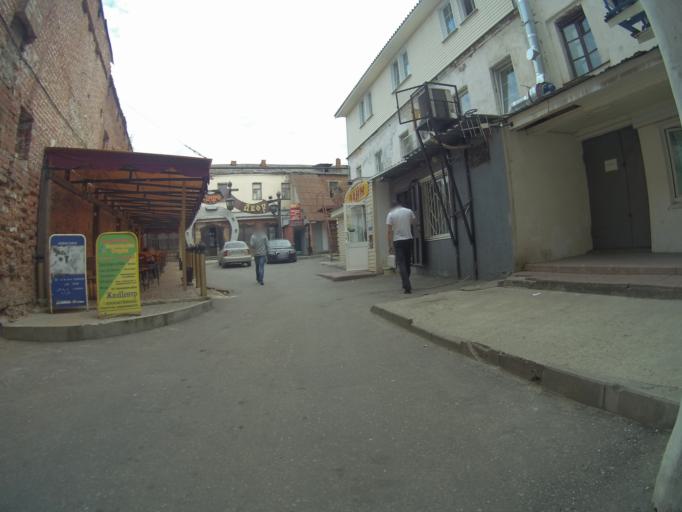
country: RU
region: Vladimir
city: Vladimir
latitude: 56.1271
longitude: 40.3994
